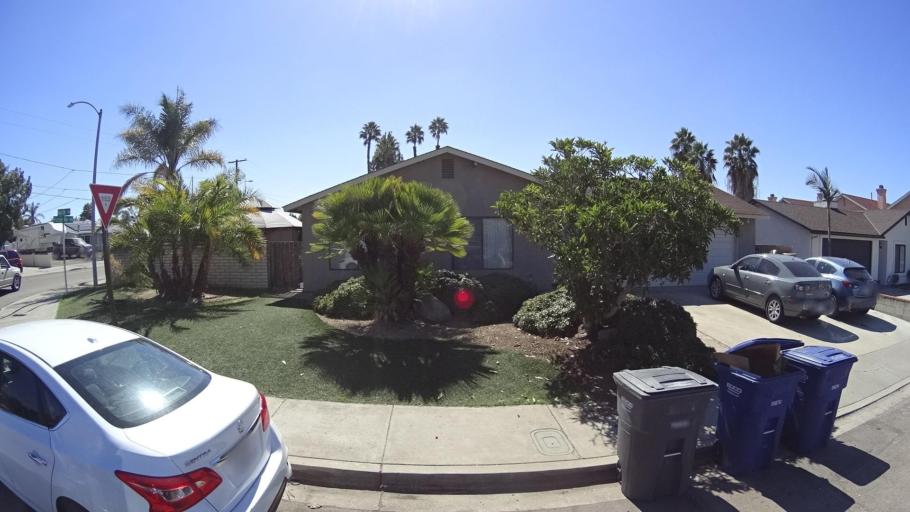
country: US
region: California
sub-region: San Diego County
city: El Cajon
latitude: 32.8115
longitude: -116.9555
